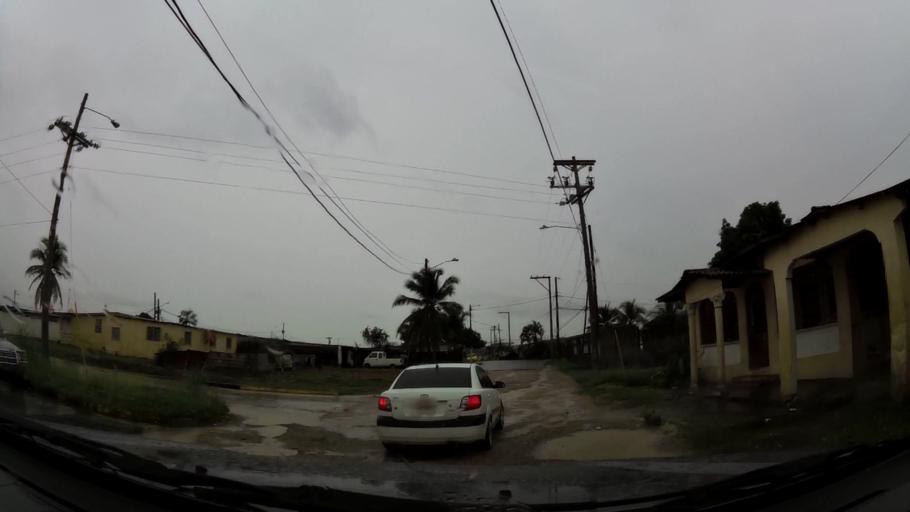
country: PA
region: Colon
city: Sabanitas
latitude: 9.3497
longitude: -79.7991
